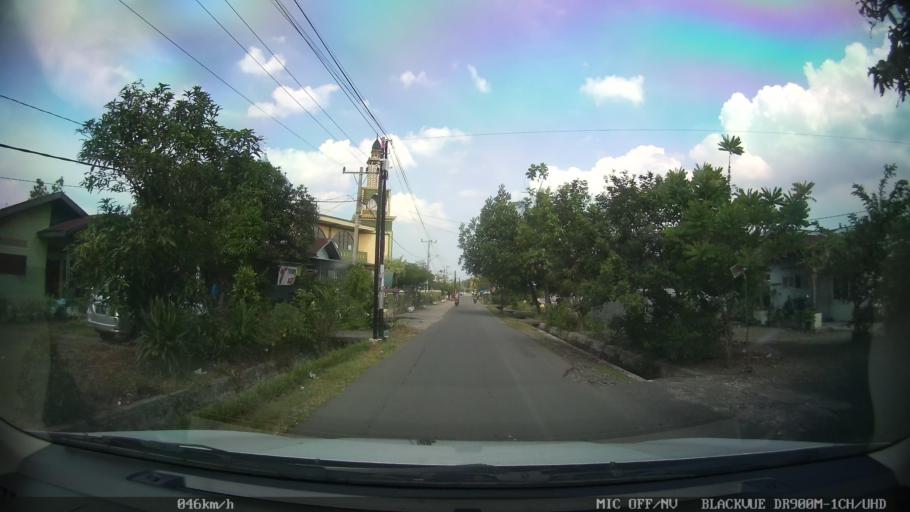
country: ID
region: North Sumatra
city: Binjai
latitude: 3.6134
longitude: 98.5296
